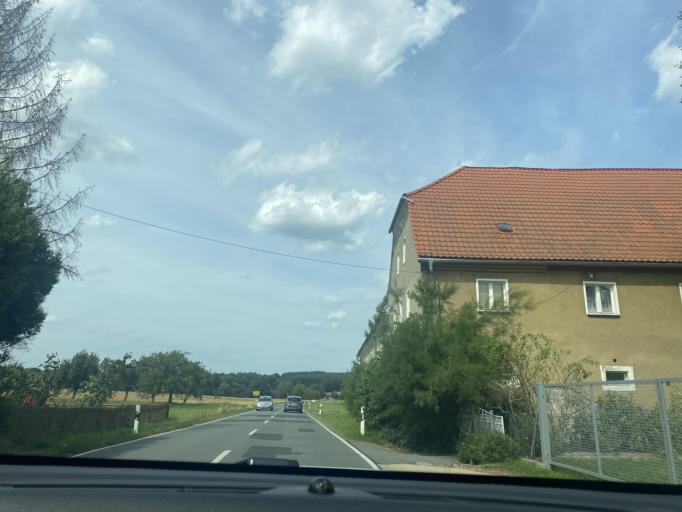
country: DE
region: Saxony
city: Grosshennersdorf
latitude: 50.9982
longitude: 14.7942
